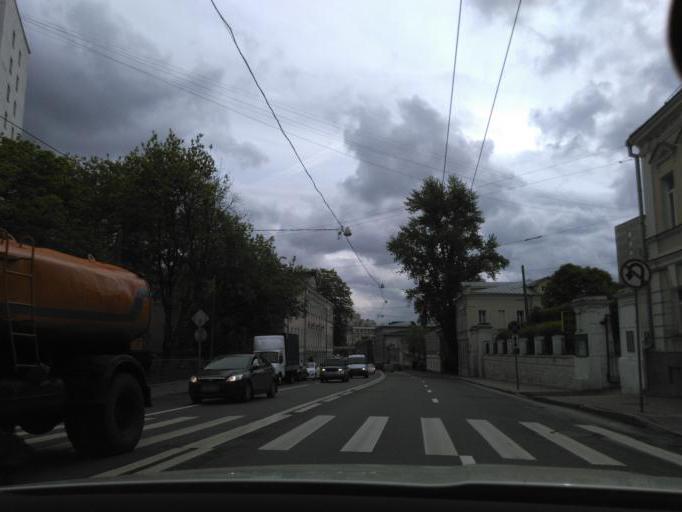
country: RU
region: Moscow
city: Zamoskvorech'ye
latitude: 55.7479
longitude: 37.6494
